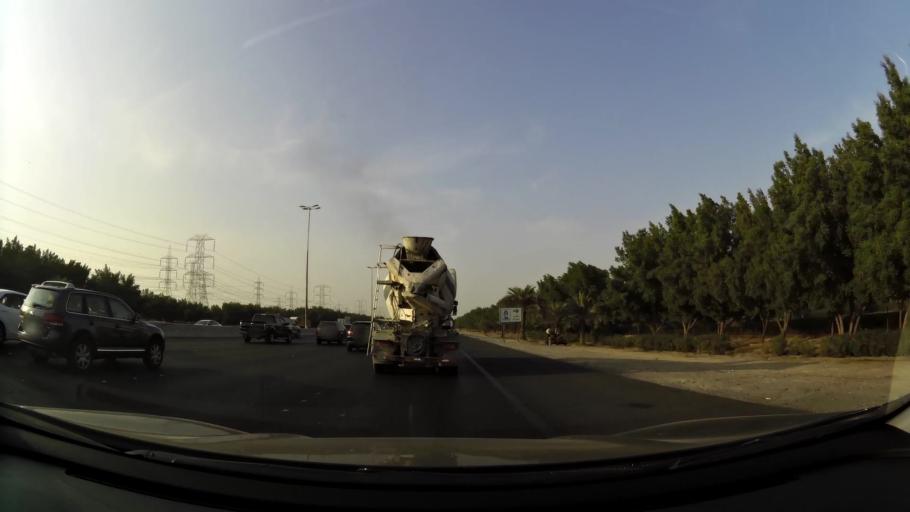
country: KW
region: Mubarak al Kabir
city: Sabah as Salim
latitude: 29.2248
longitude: 48.0544
